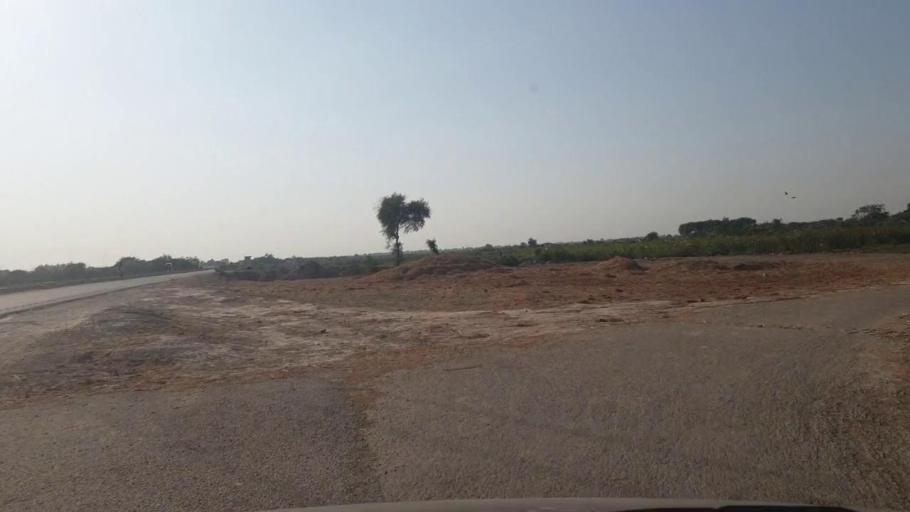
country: PK
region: Sindh
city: Badin
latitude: 24.6548
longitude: 68.8120
